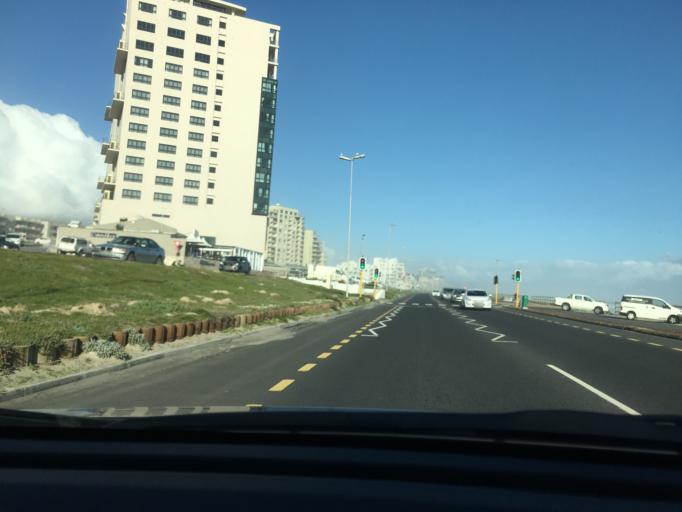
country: ZA
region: Western Cape
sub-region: City of Cape Town
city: Sunset Beach
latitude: -33.8095
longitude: 18.4683
